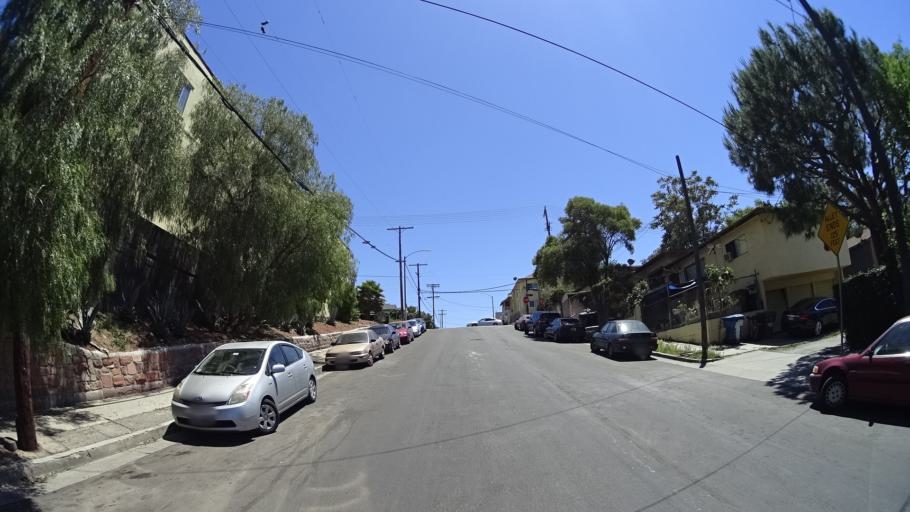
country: US
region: California
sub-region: Los Angeles County
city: Echo Park
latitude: 34.0635
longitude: -118.2580
